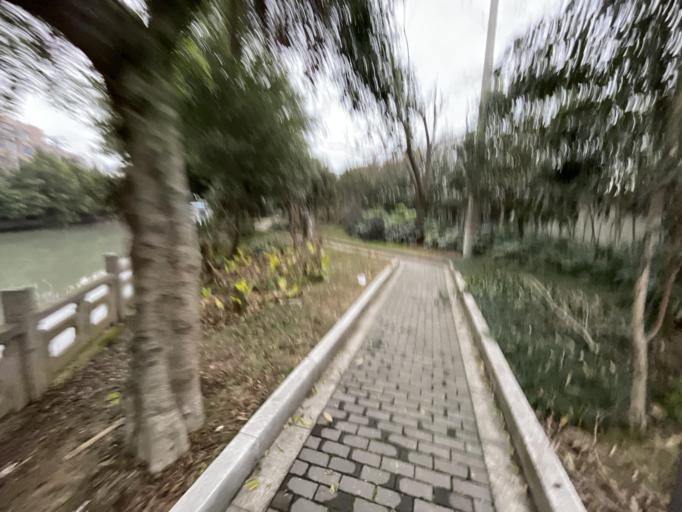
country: CN
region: Zhejiang Sheng
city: Louqiao
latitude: 27.9825
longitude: 120.6194
